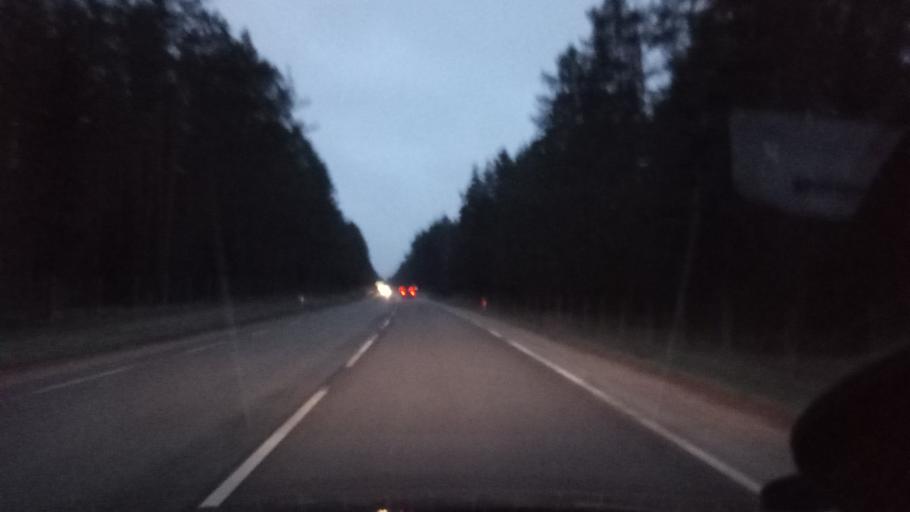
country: LT
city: Trakai
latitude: 54.5257
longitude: 24.9835
